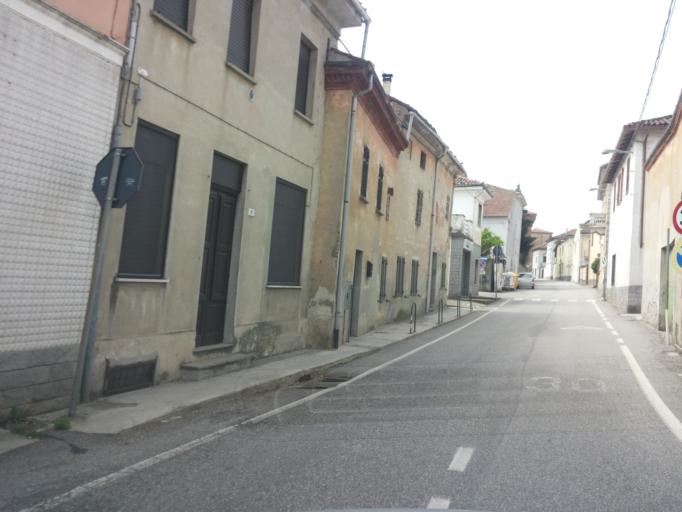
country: IT
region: Piedmont
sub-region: Provincia di Alessandria
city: Mirabello Monferrato
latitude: 45.0348
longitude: 8.5247
